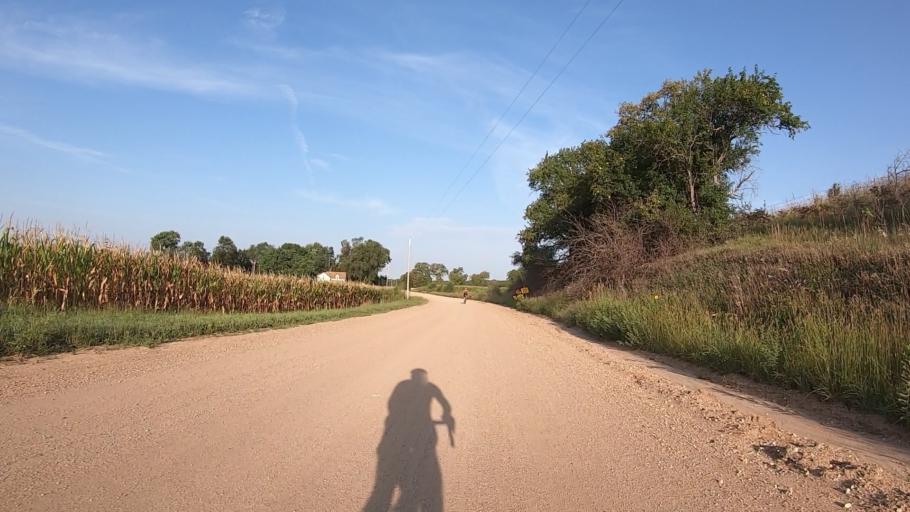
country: US
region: Kansas
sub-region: Marshall County
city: Blue Rapids
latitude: 39.7262
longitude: -96.7903
